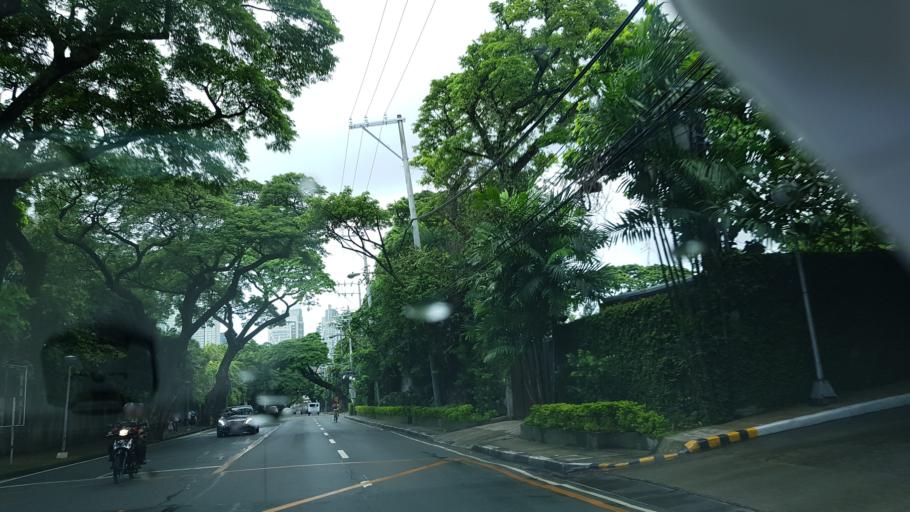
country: PH
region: Metro Manila
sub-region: Makati City
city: Makati City
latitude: 14.5480
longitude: 121.0335
